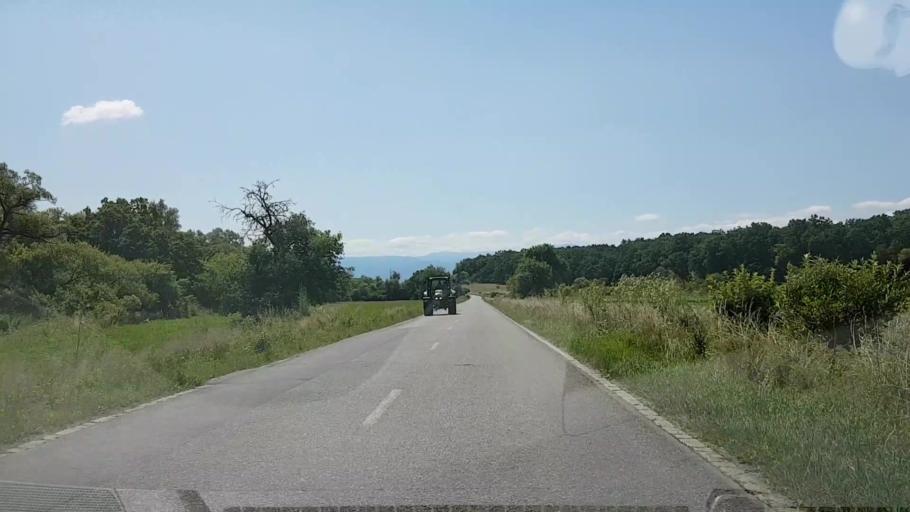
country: RO
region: Brasov
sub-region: Comuna Cincu
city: Cincu
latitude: 45.8756
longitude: 24.8189
